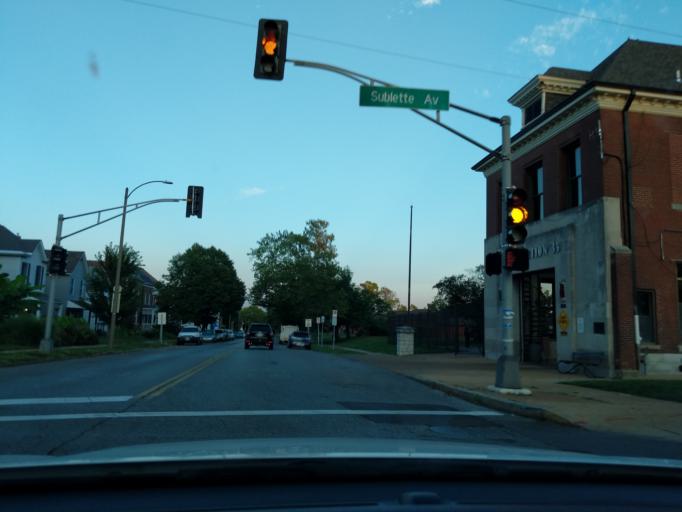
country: US
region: Missouri
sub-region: Saint Louis County
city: Maplewood
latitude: 38.6062
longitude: -90.2814
